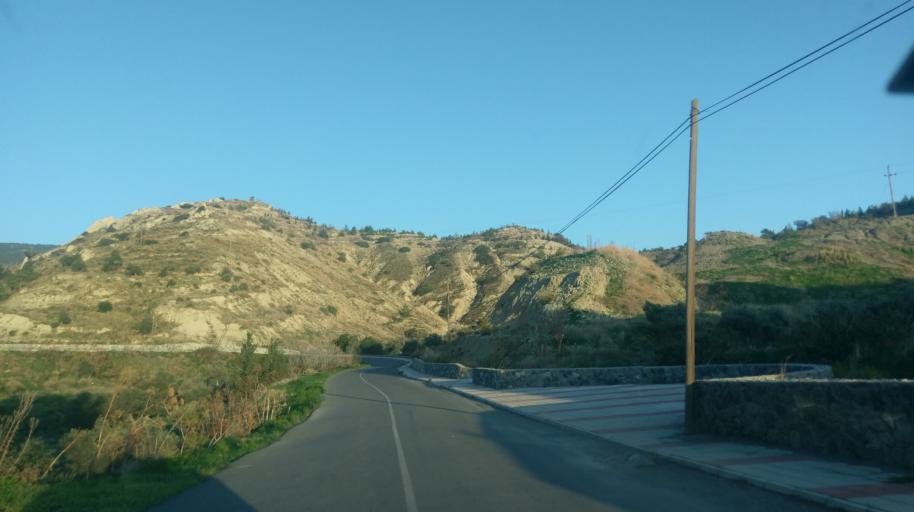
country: CY
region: Lefkosia
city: Nicosia
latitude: 35.2637
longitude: 33.4863
